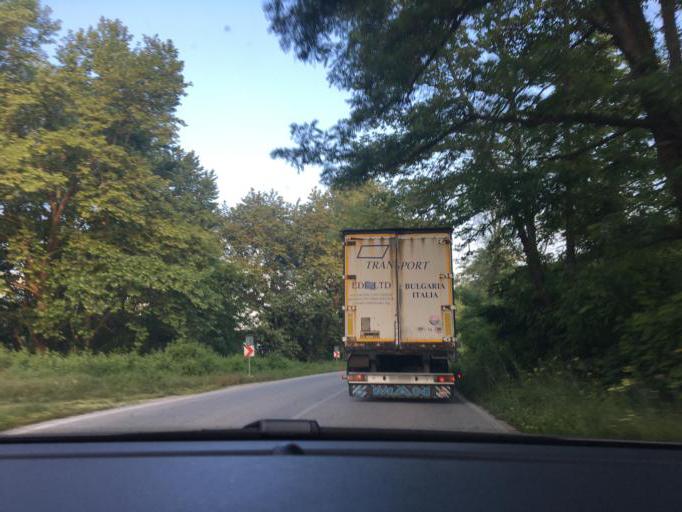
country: BG
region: Blagoevgrad
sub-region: Obshtina Petrich
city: Petrich
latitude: 41.3985
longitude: 23.0675
